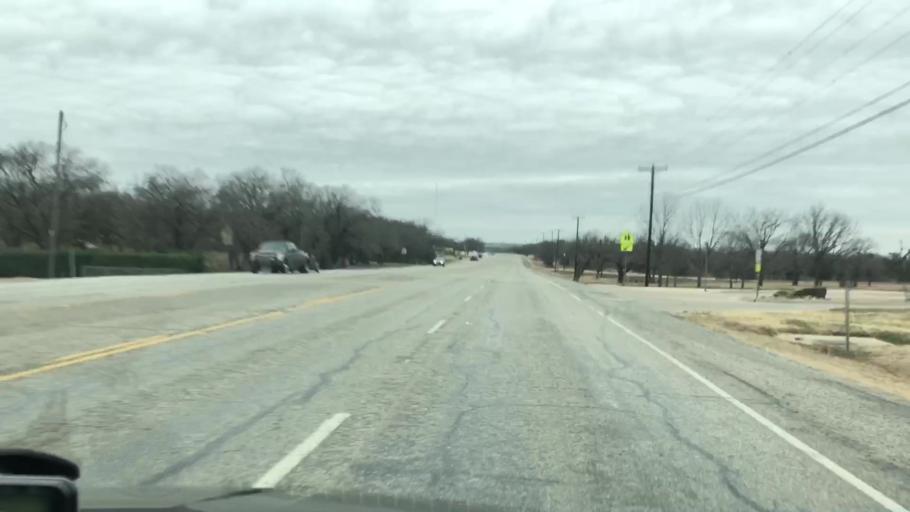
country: US
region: Texas
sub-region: Jack County
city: Jacksboro
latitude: 33.2276
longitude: -98.1701
